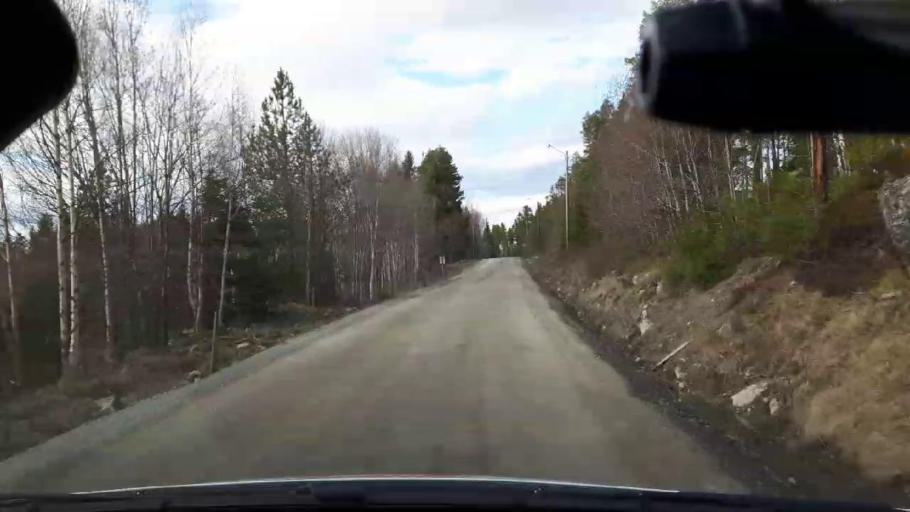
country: SE
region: Jaemtland
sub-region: Bergs Kommun
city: Hoverberg
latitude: 62.8846
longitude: 14.6582
